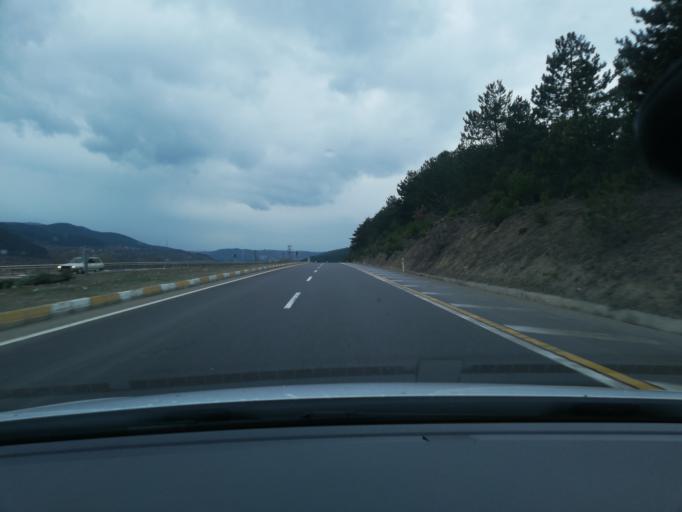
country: TR
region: Bolu
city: Yenicaga
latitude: 40.7457
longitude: 31.8688
